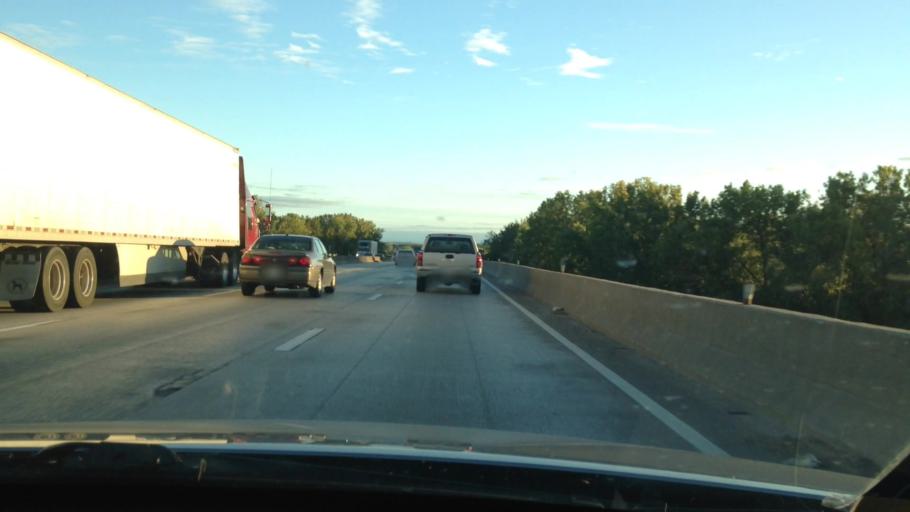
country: US
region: Missouri
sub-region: Clay County
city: Claycomo
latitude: 39.1509
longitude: -94.4984
